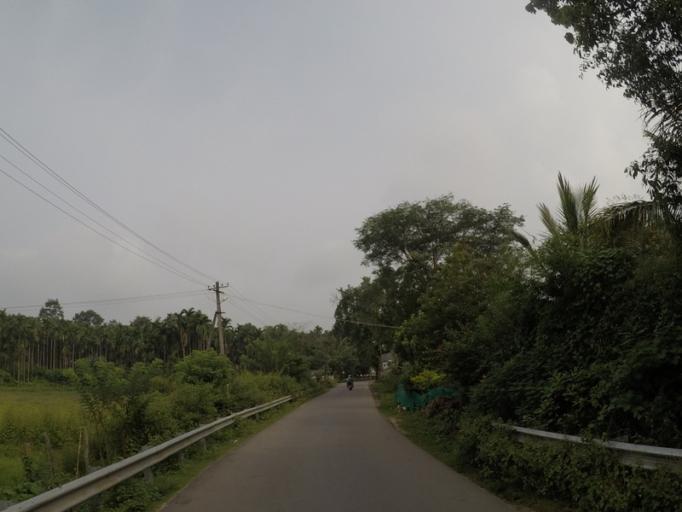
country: IN
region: Karnataka
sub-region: Chikmagalur
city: Chikmagalur
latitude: 13.3526
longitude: 75.5381
